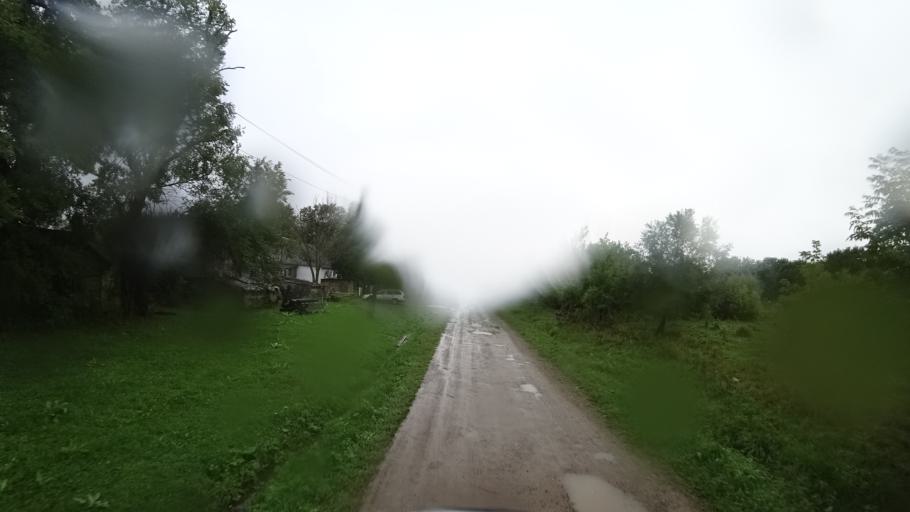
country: RU
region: Primorskiy
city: Monastyrishche
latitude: 44.2530
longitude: 132.4265
